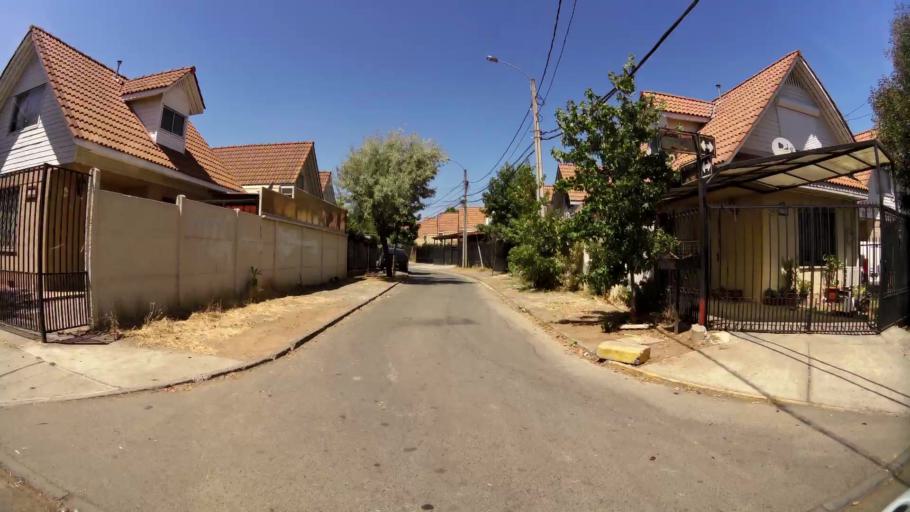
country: CL
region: Maule
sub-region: Provincia de Talca
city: Talca
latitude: -35.4313
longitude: -71.6251
